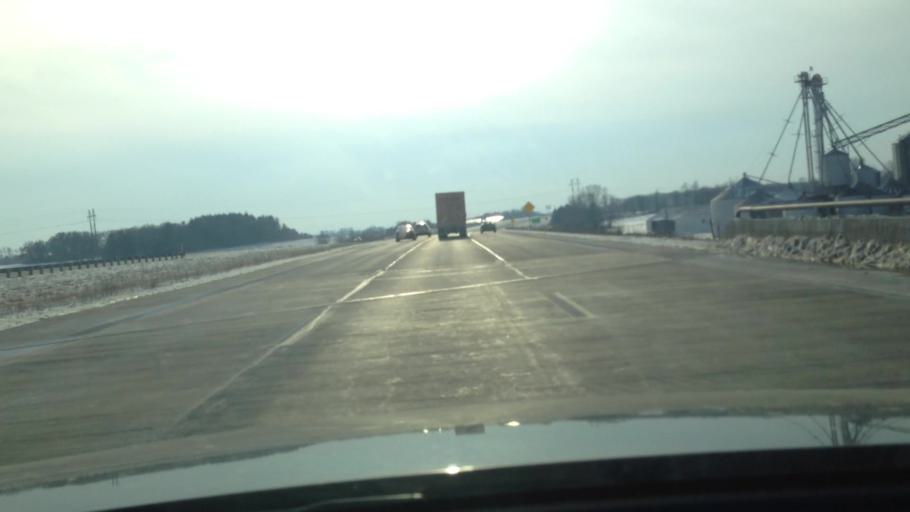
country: US
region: Wisconsin
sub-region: Walworth County
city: Elkhorn
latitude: 42.7061
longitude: -88.4847
